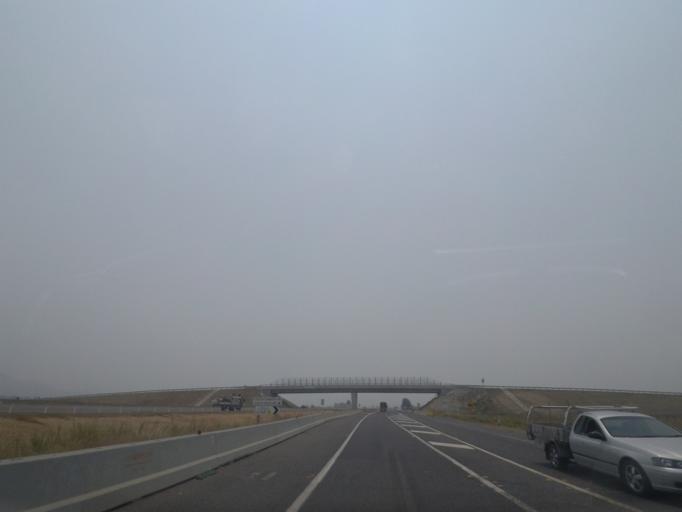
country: AU
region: New South Wales
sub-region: Clarence Valley
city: Maclean
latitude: -29.3944
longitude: 153.2394
